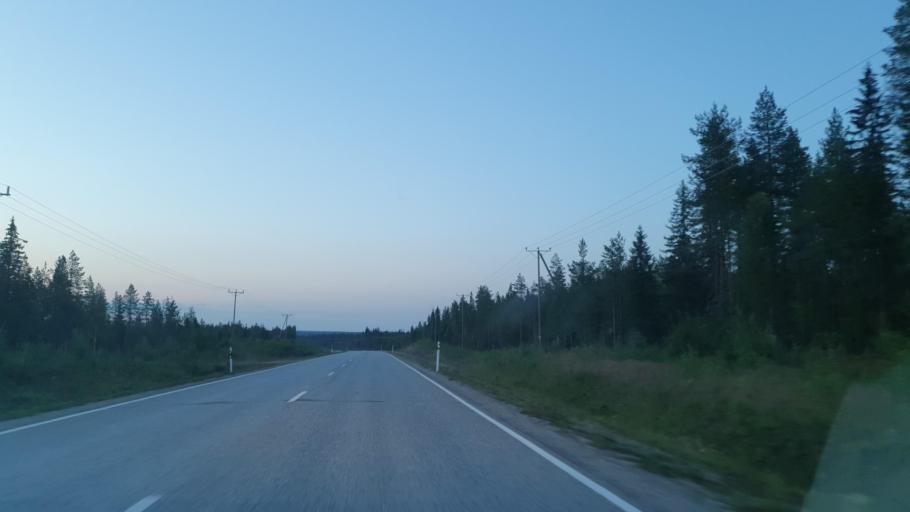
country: FI
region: Kainuu
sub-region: Kehys-Kainuu
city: Suomussalmi
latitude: 65.1064
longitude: 28.9094
